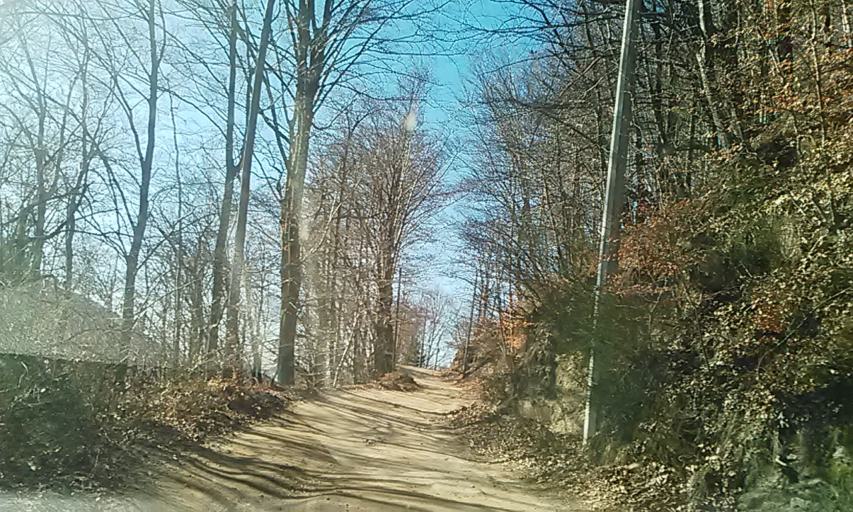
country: IT
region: Piedmont
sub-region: Provincia di Vercelli
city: Civiasco
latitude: 45.7883
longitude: 8.2959
